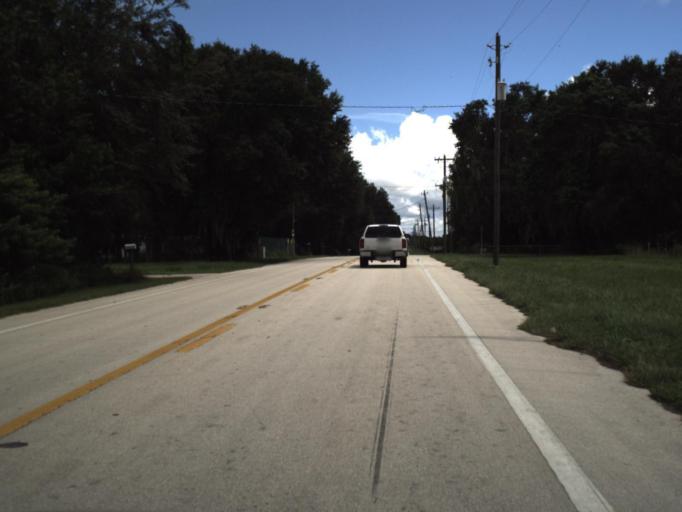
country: US
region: Florida
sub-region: Polk County
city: Fort Meade
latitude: 27.7481
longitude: -81.7616
